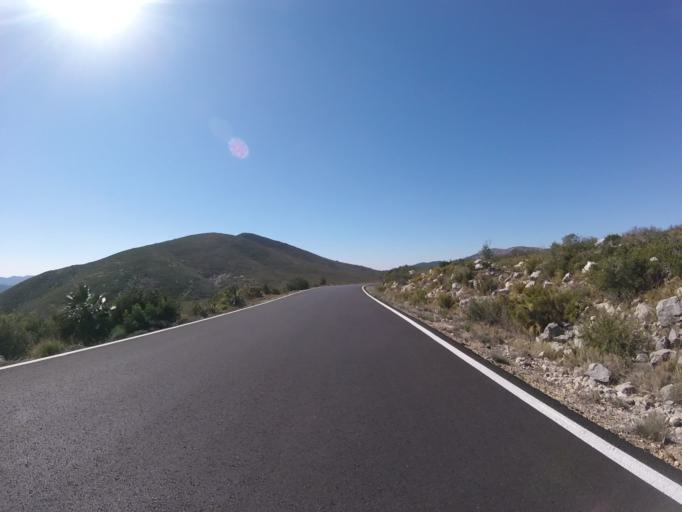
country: ES
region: Valencia
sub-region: Provincia de Castello
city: Cervera del Maestre
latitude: 40.4062
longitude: 0.2185
